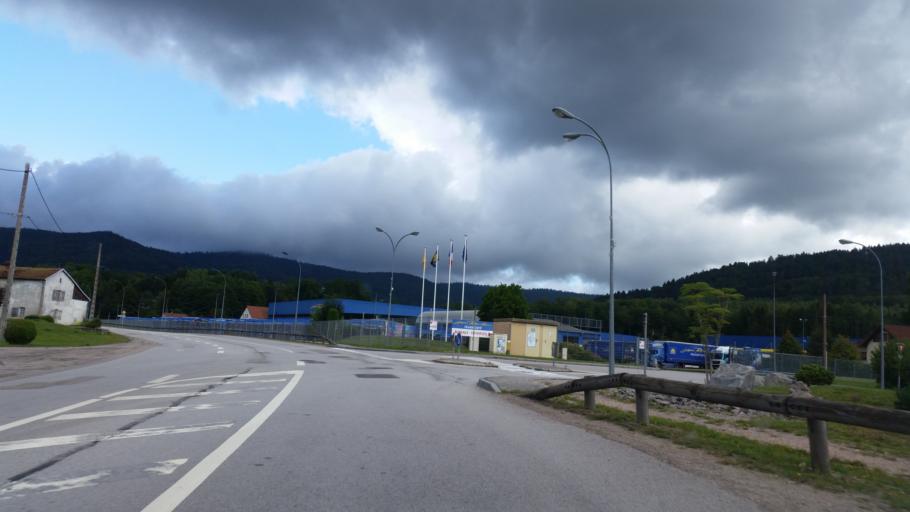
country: FR
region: Lorraine
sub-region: Departement des Vosges
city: Le Syndicat
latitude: 48.0279
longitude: 6.6807
